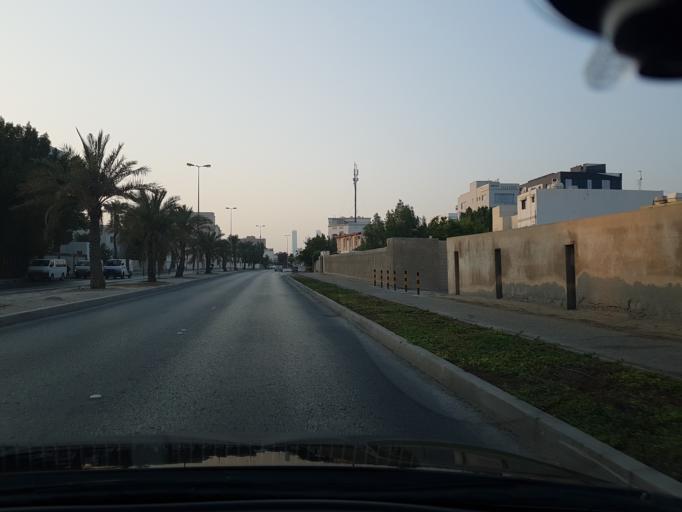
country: BH
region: Manama
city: Manama
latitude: 26.2090
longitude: 50.5843
